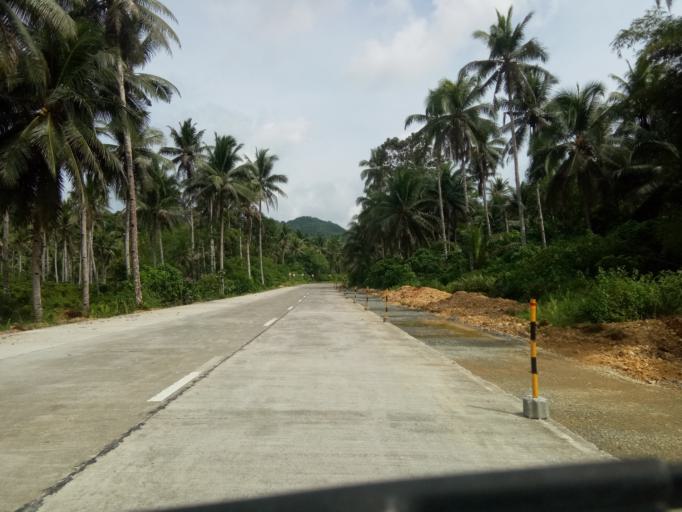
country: PH
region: Caraga
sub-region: Province of Surigao del Norte
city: Dapa
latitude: 9.8011
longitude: 126.0660
